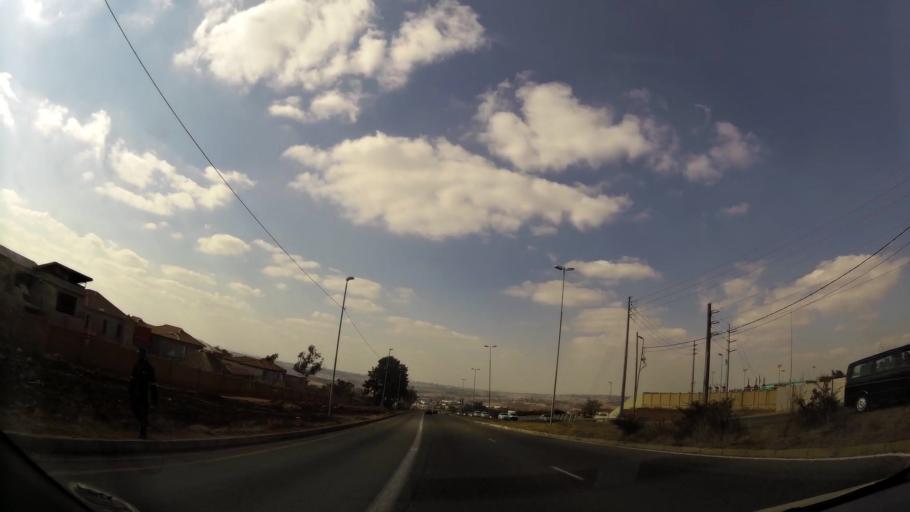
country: ZA
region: Gauteng
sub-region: West Rand District Municipality
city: Muldersdriseloop
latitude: -26.0668
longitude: 27.8241
